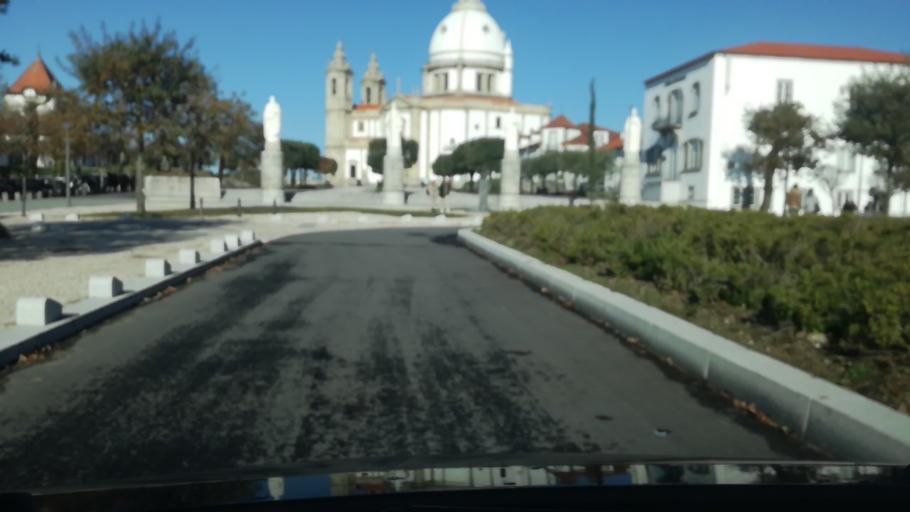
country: PT
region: Braga
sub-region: Braga
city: Braga
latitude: 41.5403
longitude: -8.3689
